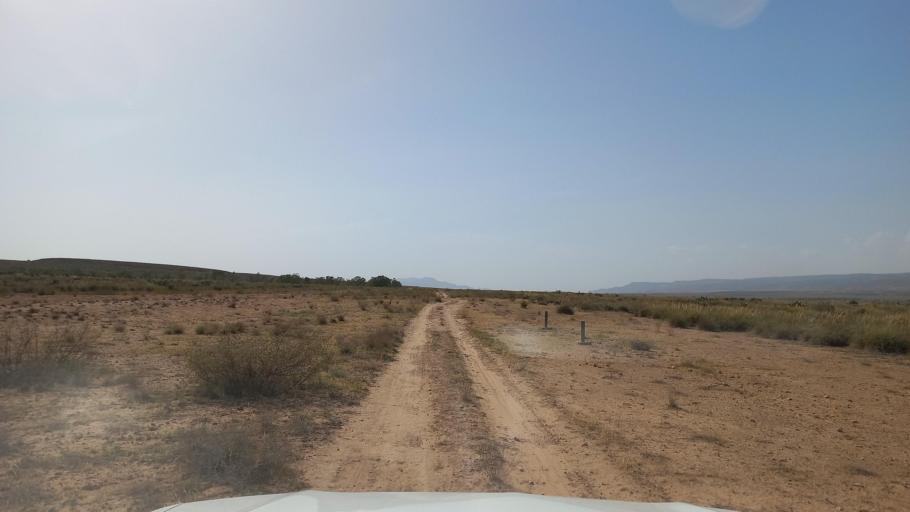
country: TN
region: Al Qasrayn
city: Kasserine
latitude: 35.2142
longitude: 9.0008
